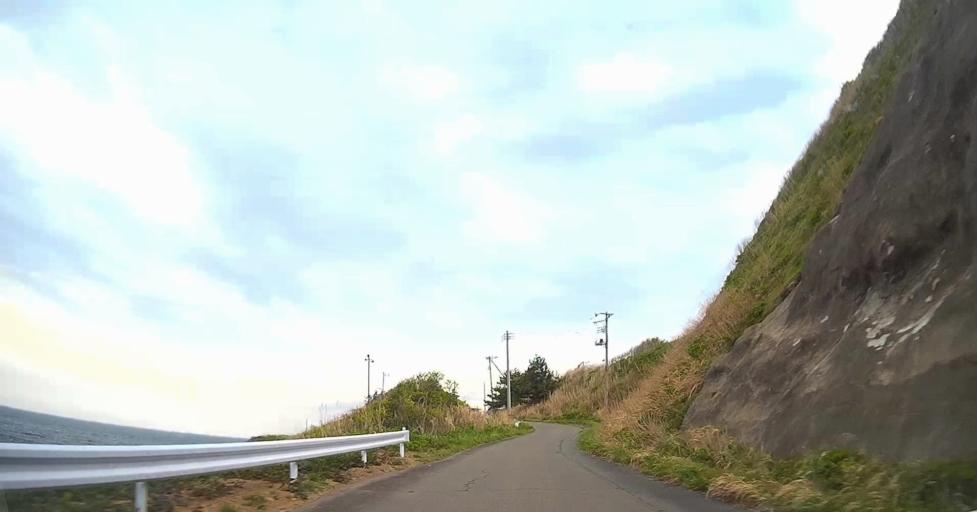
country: JP
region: Aomori
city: Shimokizukuri
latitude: 41.2425
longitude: 140.3422
